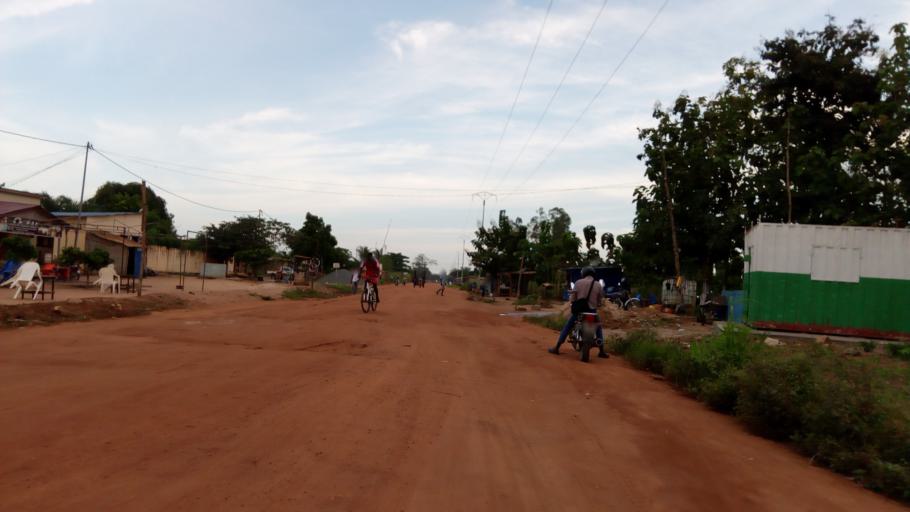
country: TG
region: Maritime
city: Lome
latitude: 6.2553
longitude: 1.1391
